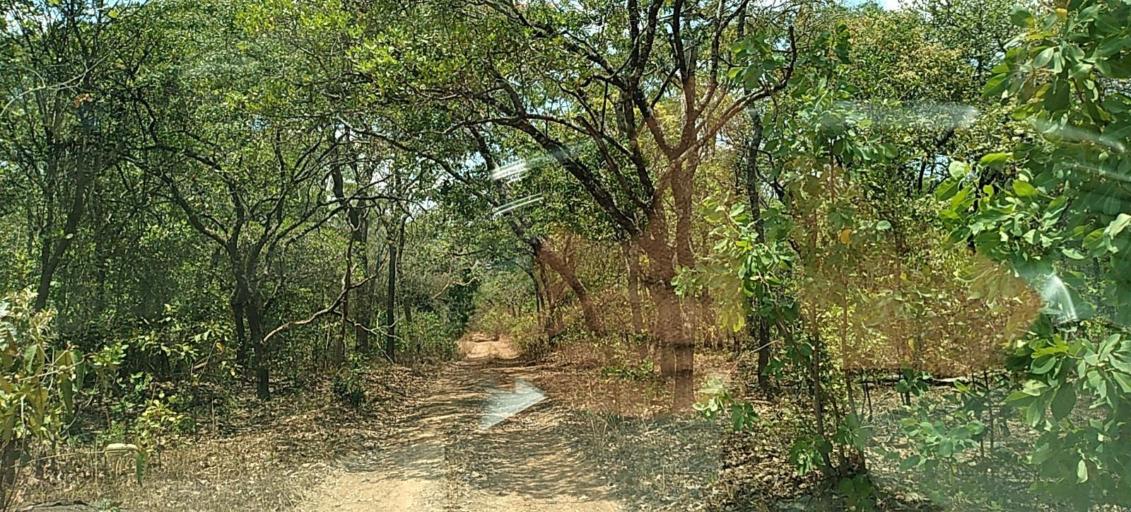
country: ZM
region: Copperbelt
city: Chililabombwe
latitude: -12.4701
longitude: 27.7001
